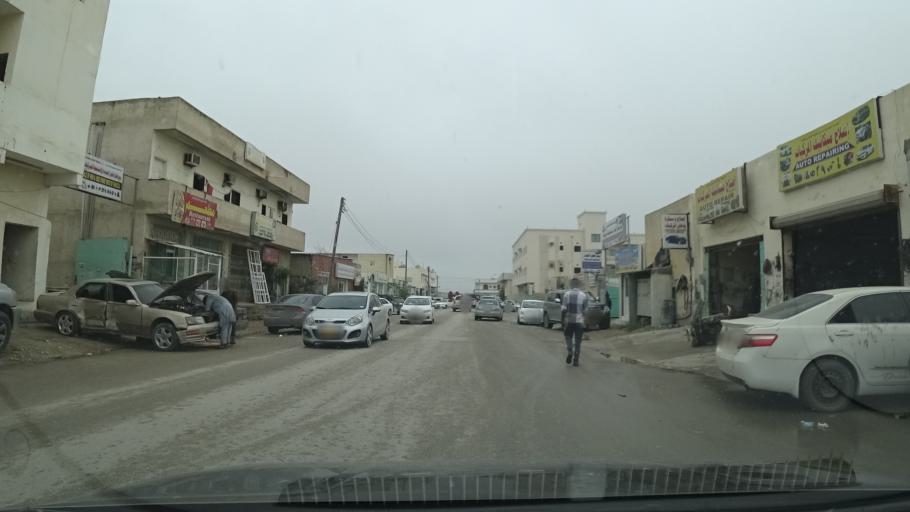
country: OM
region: Zufar
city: Salalah
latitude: 17.0231
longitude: 54.0503
